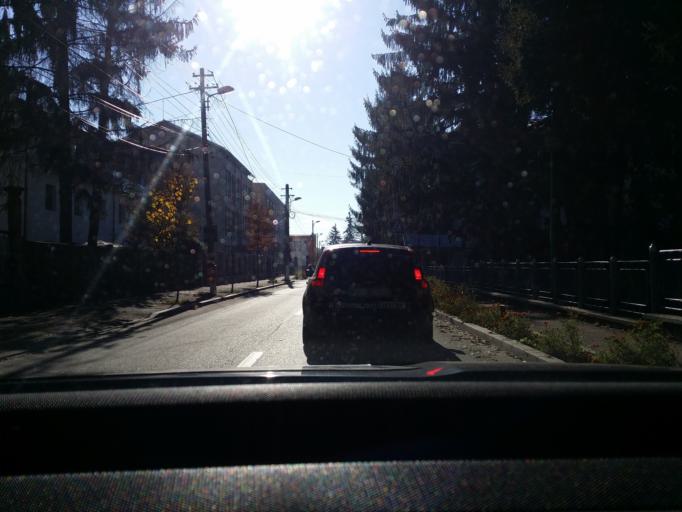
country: RO
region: Prahova
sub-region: Municipiul Campina
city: Campina
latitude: 45.1199
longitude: 25.7353
